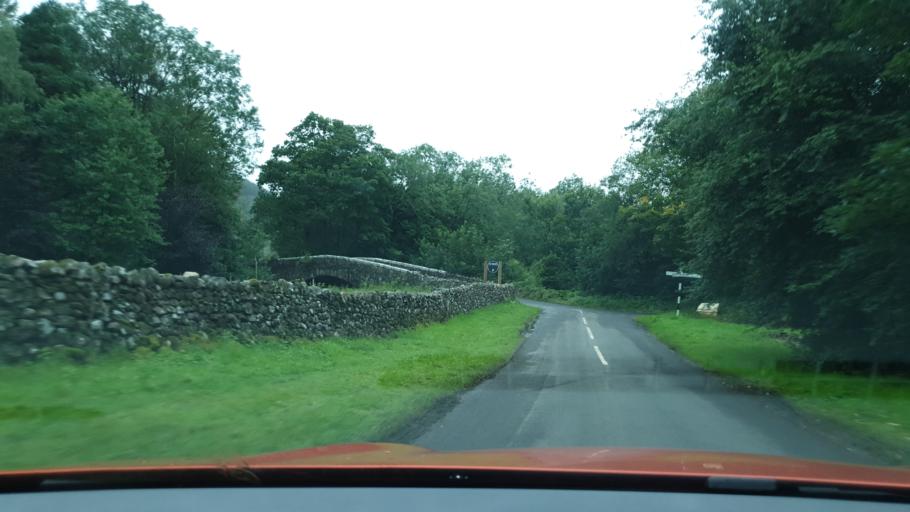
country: GB
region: England
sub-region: Cumbria
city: Seascale
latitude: 54.4222
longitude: -3.3441
